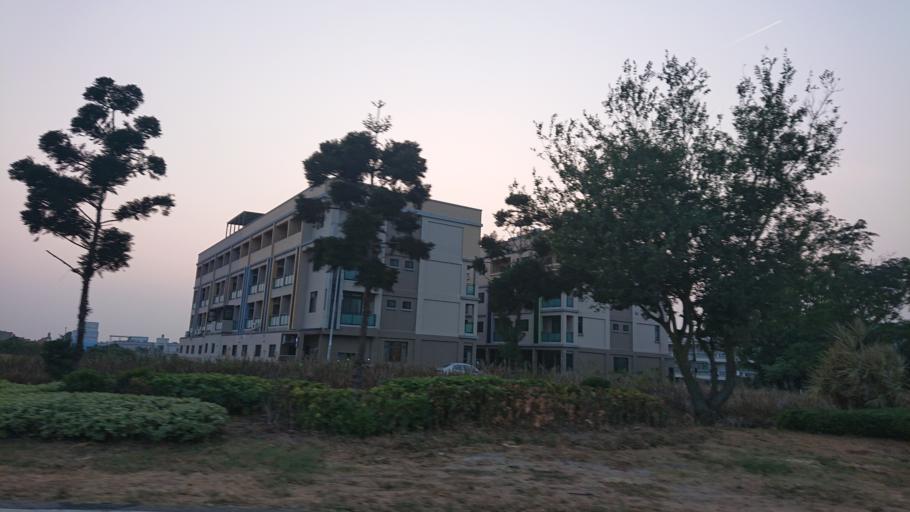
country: TW
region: Fukien
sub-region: Kinmen
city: Jincheng
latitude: 24.4455
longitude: 118.3192
